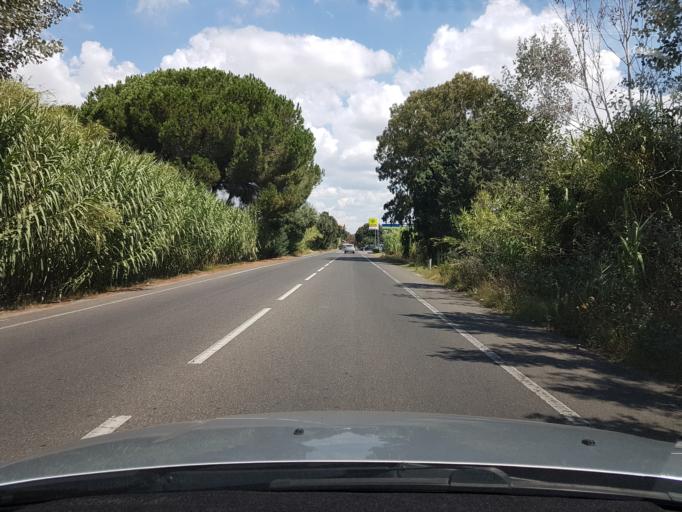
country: IT
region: Sardinia
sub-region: Provincia di Oristano
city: Donigala Fenugheddu
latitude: 39.9239
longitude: 8.5741
